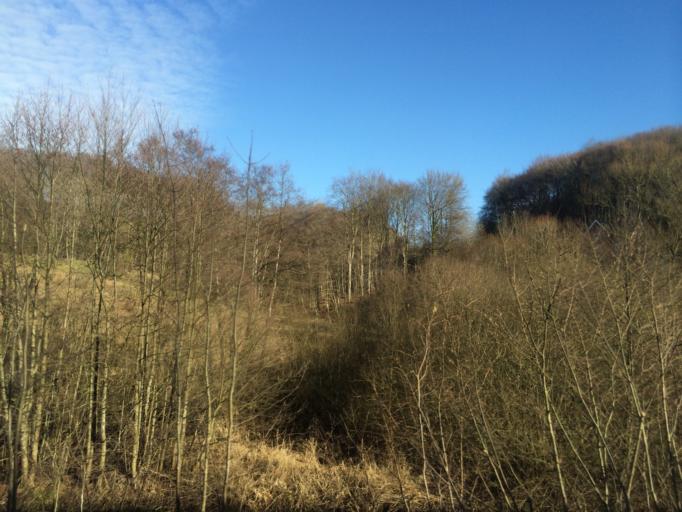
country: DK
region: South Denmark
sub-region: Vejle Kommune
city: Vejle
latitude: 55.7574
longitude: 9.5310
